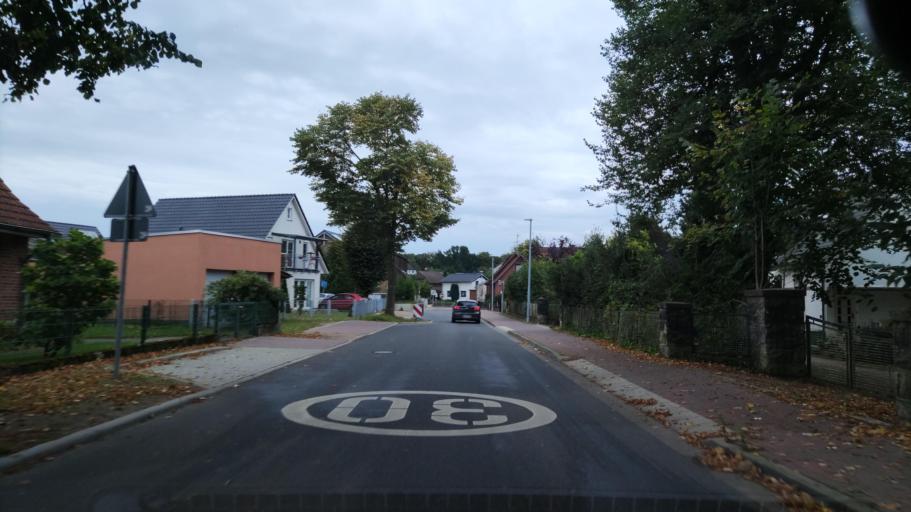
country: DE
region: Schleswig-Holstein
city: Trittau
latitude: 53.6044
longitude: 10.4101
